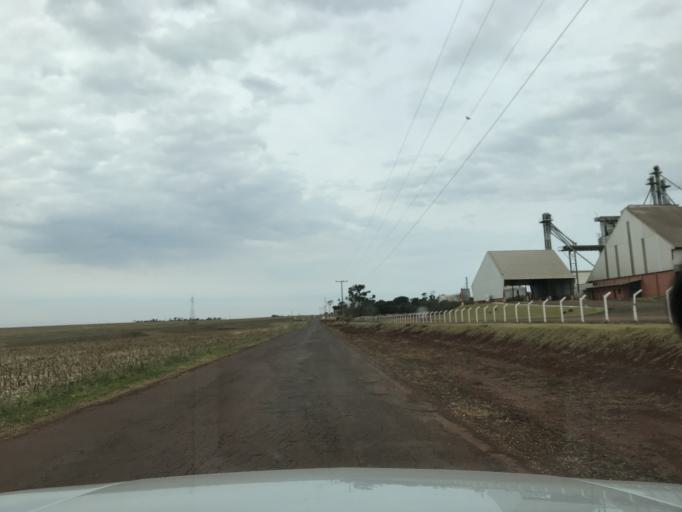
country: BR
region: Parana
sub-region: Palotina
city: Palotina
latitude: -24.2848
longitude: -53.7981
